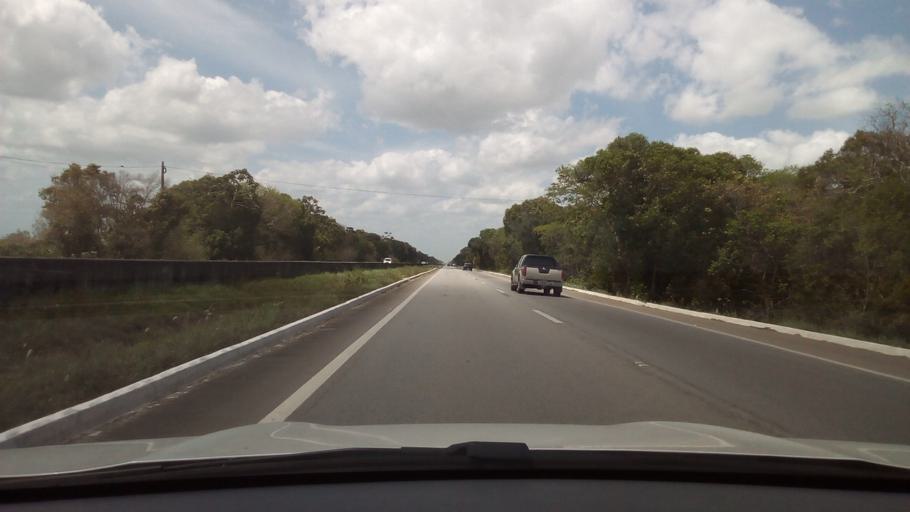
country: BR
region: Paraiba
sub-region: Mamanguape
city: Mamanguape
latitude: -6.9210
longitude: -35.1091
